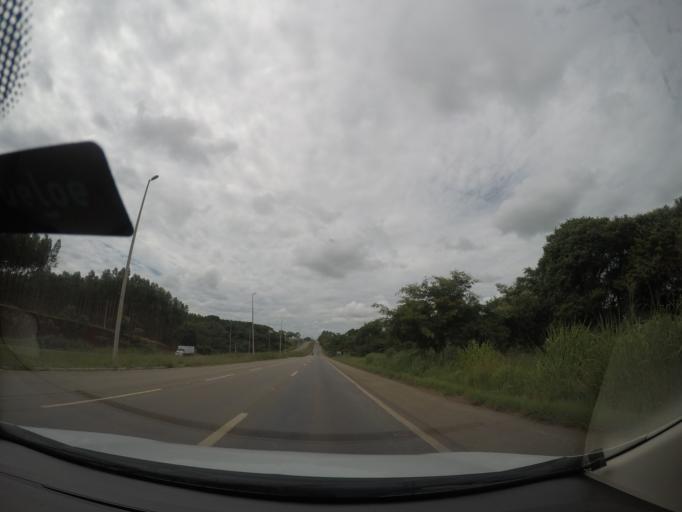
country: BR
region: Goias
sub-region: Goianira
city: Goianira
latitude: -16.4381
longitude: -49.4581
